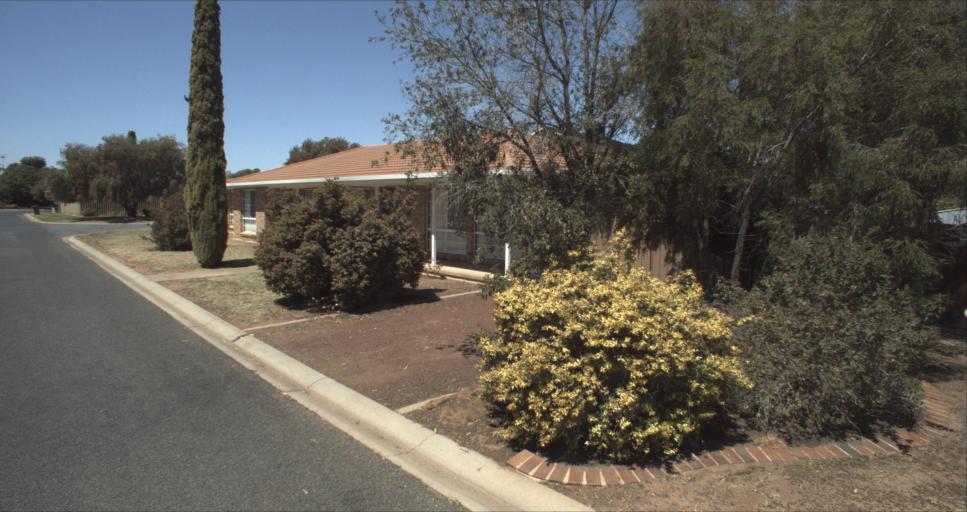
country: AU
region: New South Wales
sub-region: Leeton
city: Leeton
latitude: -34.5421
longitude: 146.4017
